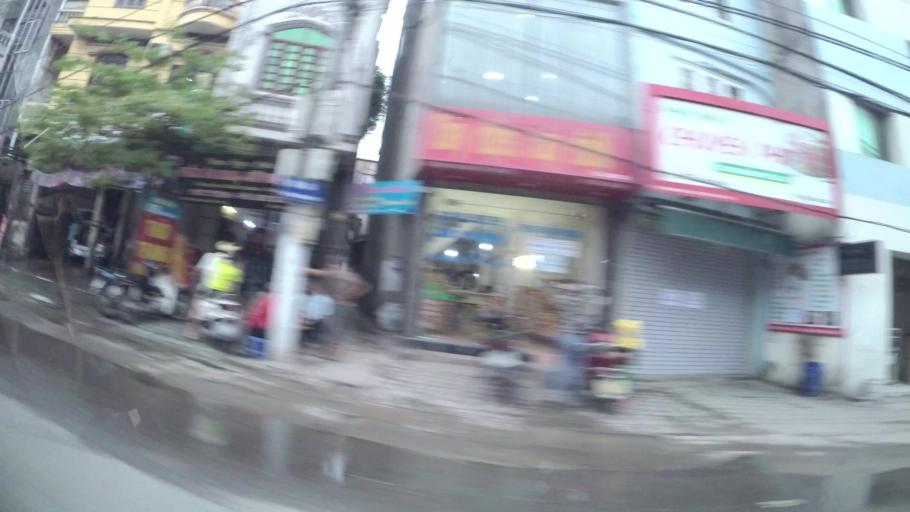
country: VN
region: Ha Noi
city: Hai BaTrung
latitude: 21.0044
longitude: 105.8693
